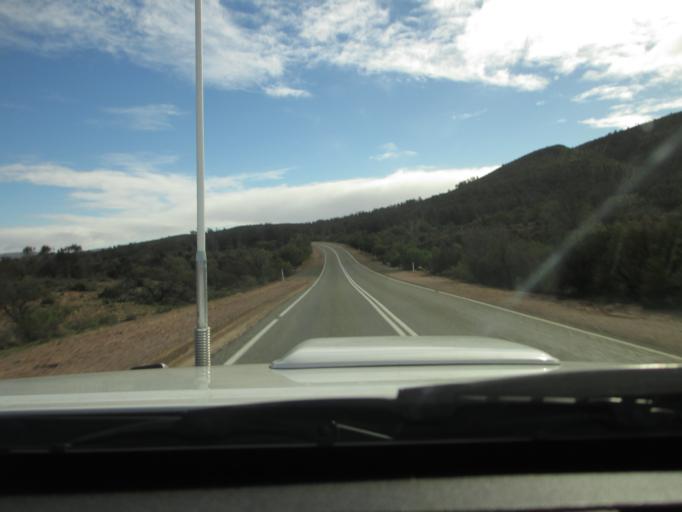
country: AU
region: South Australia
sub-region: Flinders Ranges
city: Quorn
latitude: -31.7890
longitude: 138.3538
